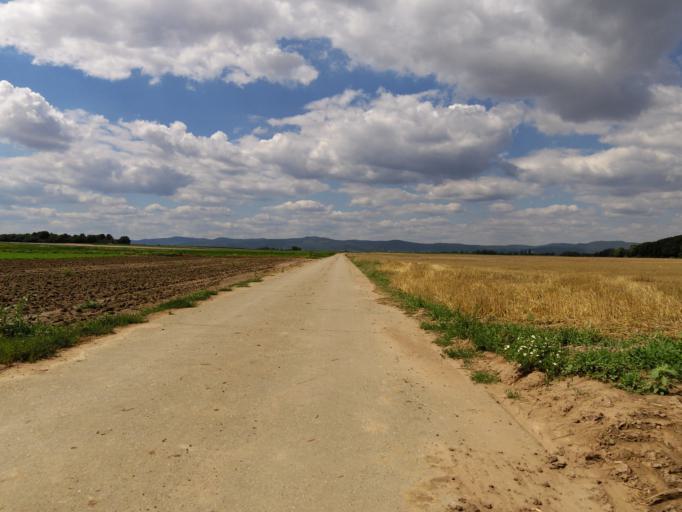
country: DE
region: Rheinland-Pfalz
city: Fussgonheim
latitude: 49.4499
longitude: 8.2886
